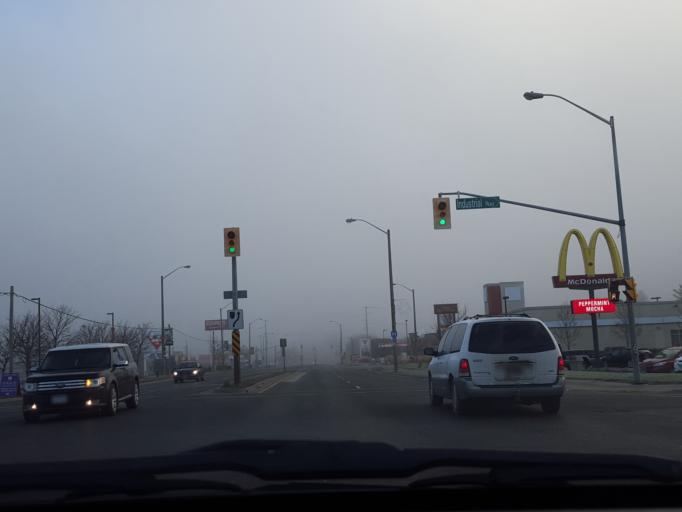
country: CA
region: Ontario
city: Angus
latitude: 44.1480
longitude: -79.8858
